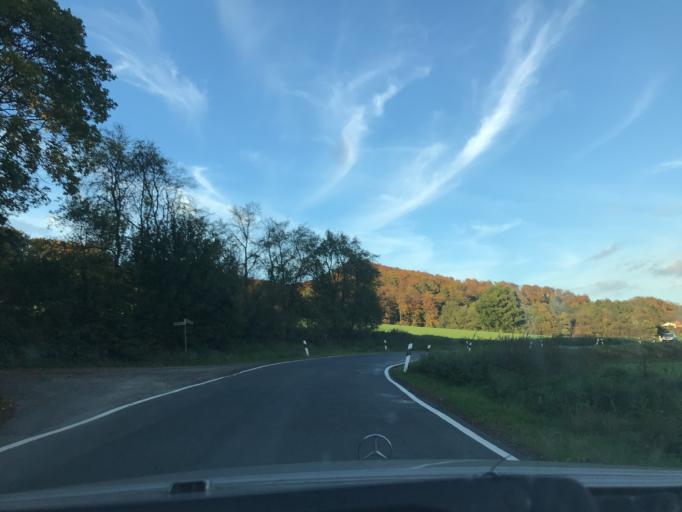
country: DE
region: Lower Saxony
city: Juhnde
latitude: 51.3978
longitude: 9.7841
